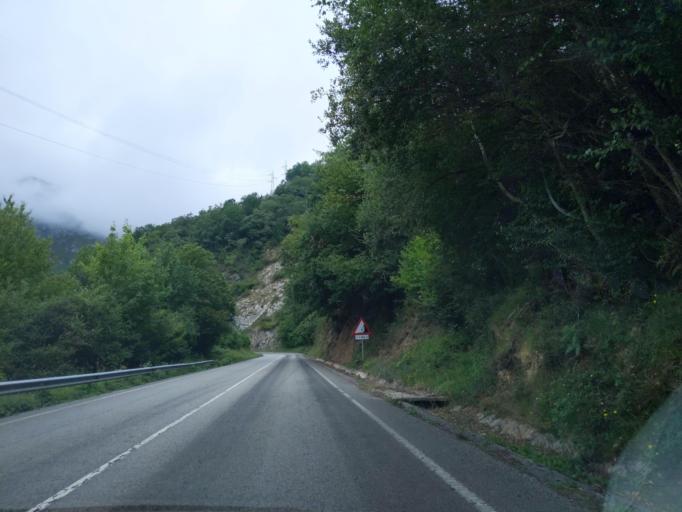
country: ES
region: Asturias
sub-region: Province of Asturias
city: Pola de Laviana
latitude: 43.2272
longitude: -5.4628
